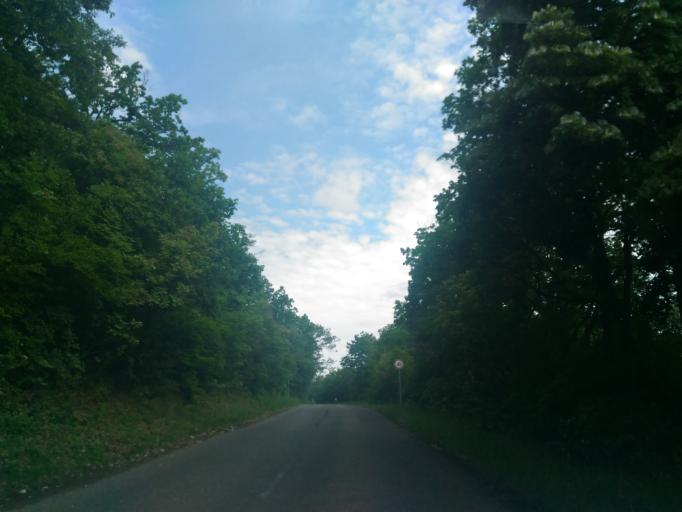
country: HU
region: Baranya
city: Pecs
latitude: 46.0992
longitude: 18.2270
